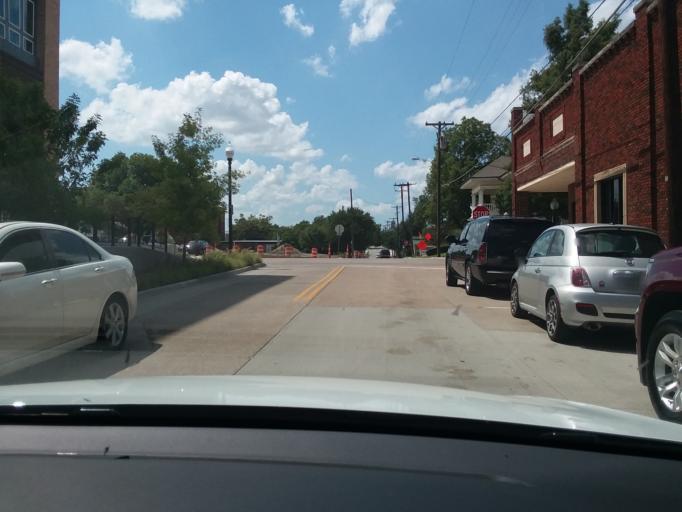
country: US
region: Texas
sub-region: Collin County
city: McKinney
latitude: 33.1959
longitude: -96.6146
